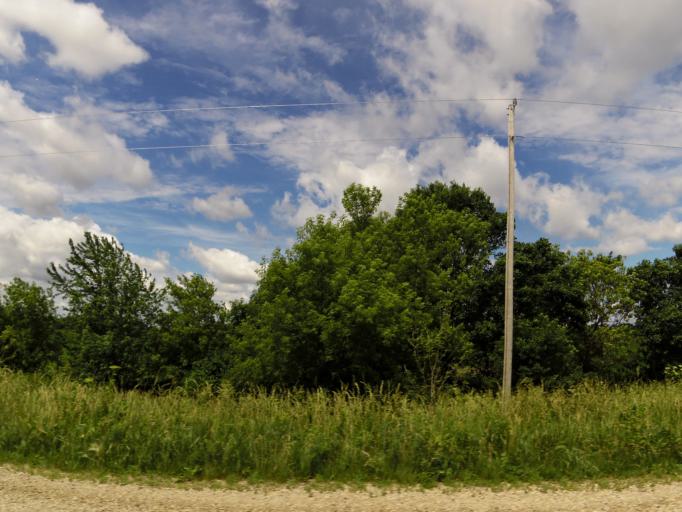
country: US
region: Iowa
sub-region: Chickasaw County
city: New Hampton
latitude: 43.2042
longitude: -92.2983
